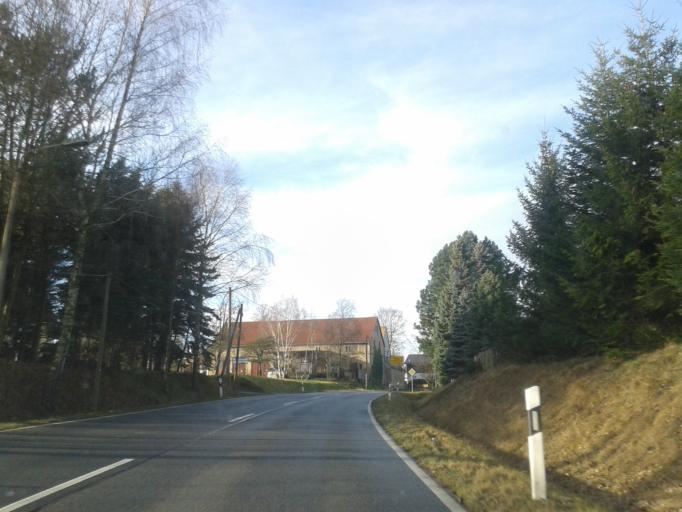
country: DE
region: Saxony
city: Eibau
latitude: 50.9738
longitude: 14.6745
